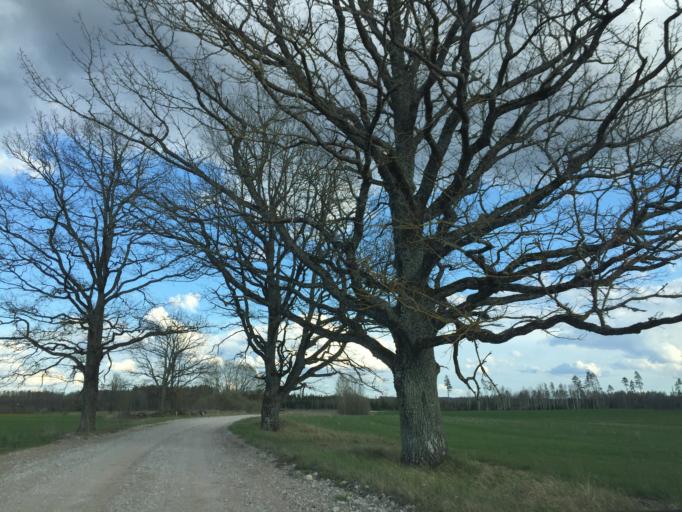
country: LV
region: Raunas
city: Rauna
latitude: 57.3694
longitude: 25.5081
